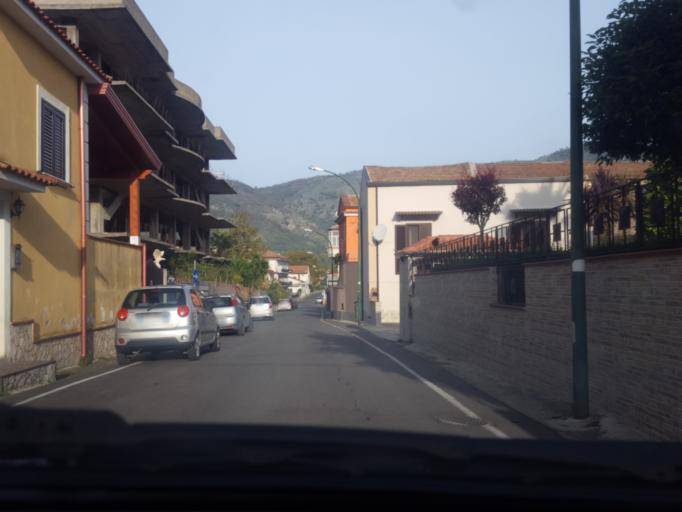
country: IT
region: Campania
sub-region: Provincia di Caserta
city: Arienzo
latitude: 41.0245
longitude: 14.4976
